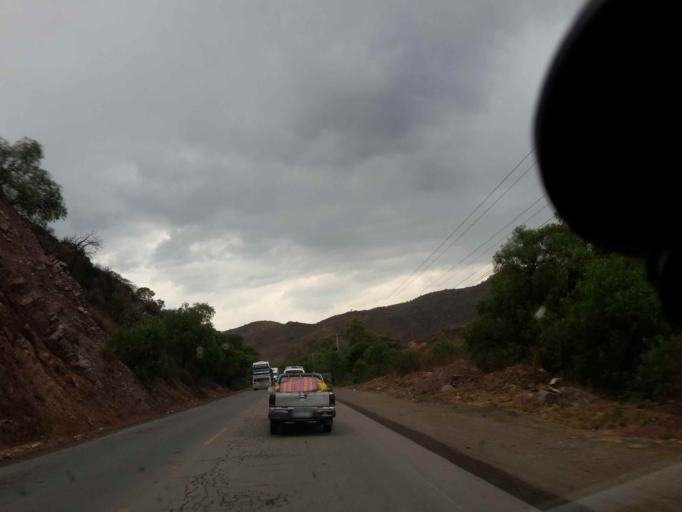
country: BO
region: Cochabamba
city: Sipe Sipe
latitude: -17.5067
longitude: -66.3341
